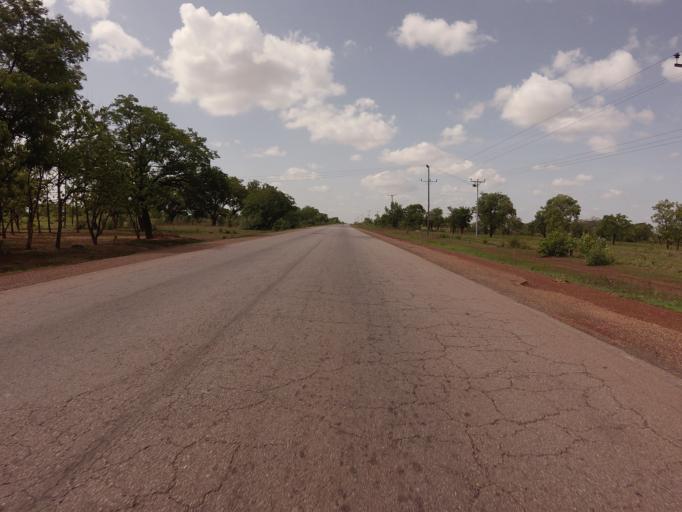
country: GH
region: Northern
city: Savelugu
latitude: 9.8797
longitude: -0.8703
